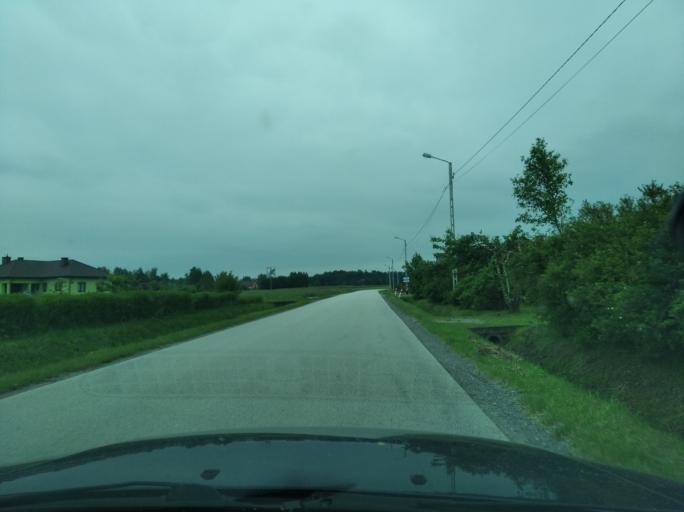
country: PL
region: Subcarpathian Voivodeship
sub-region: Powiat ropczycko-sedziszowski
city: Sedziszow Malopolski
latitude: 50.1224
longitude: 21.6732
